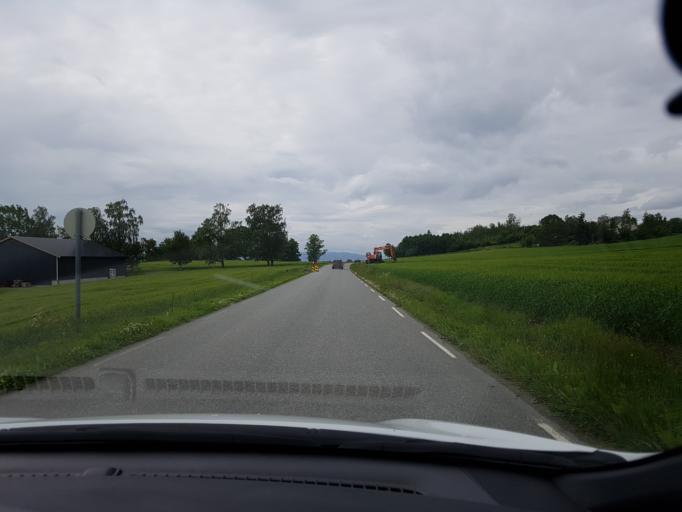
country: NO
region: Nord-Trondelag
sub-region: Frosta
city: Frosta
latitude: 63.5828
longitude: 10.7278
